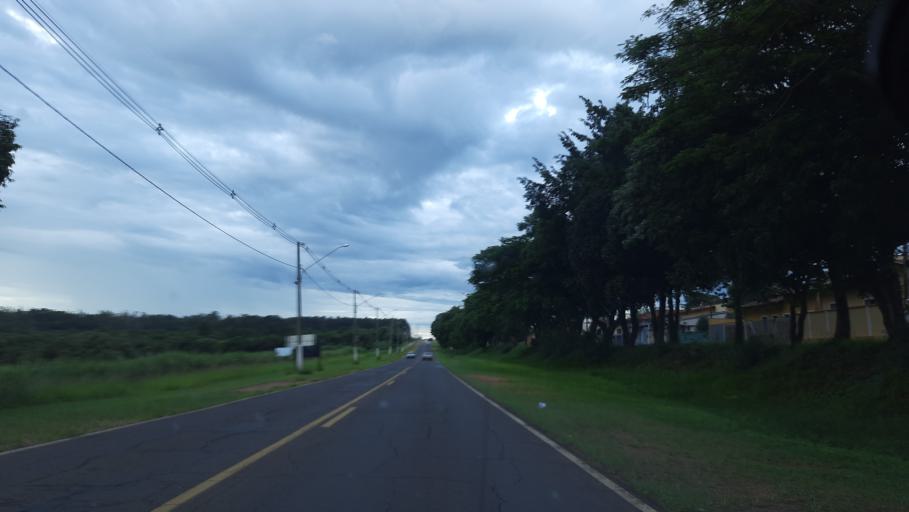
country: BR
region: Sao Paulo
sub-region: Casa Branca
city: Casa Branca
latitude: -21.7780
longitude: -47.0724
